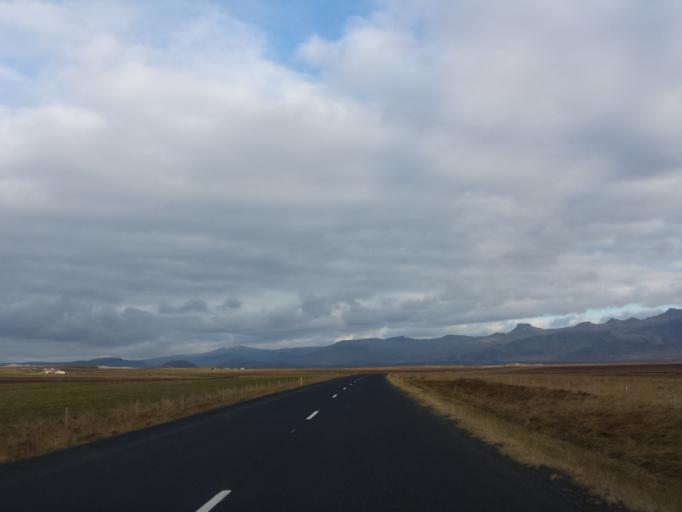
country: IS
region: West
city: Stykkisholmur
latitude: 64.8468
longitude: -22.4120
